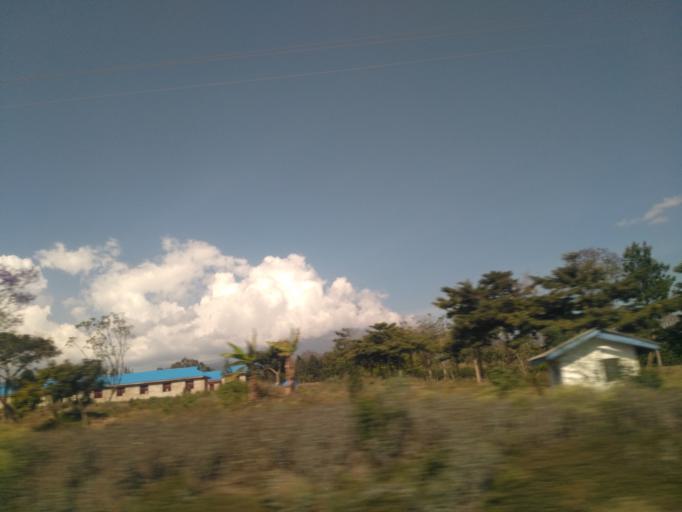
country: TZ
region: Arusha
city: Arusha
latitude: -3.2982
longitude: 36.6302
